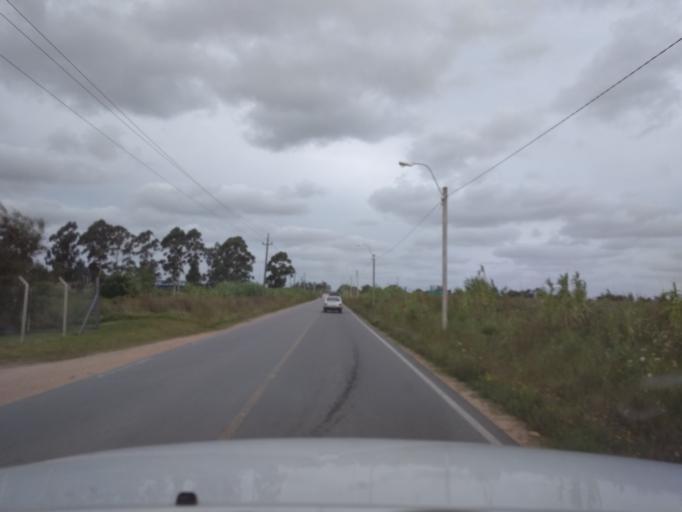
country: UY
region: Canelones
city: Colonia Nicolich
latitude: -34.7860
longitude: -56.0039
